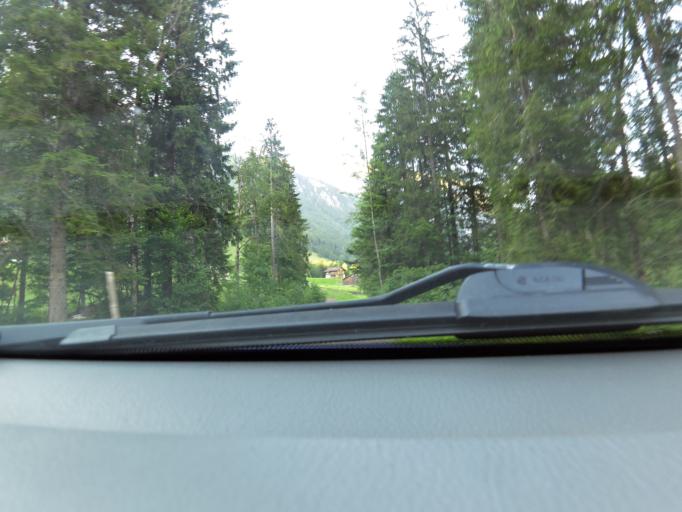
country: CH
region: Nidwalden
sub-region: Nidwalden
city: Emmetten
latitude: 46.9033
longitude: 8.5235
